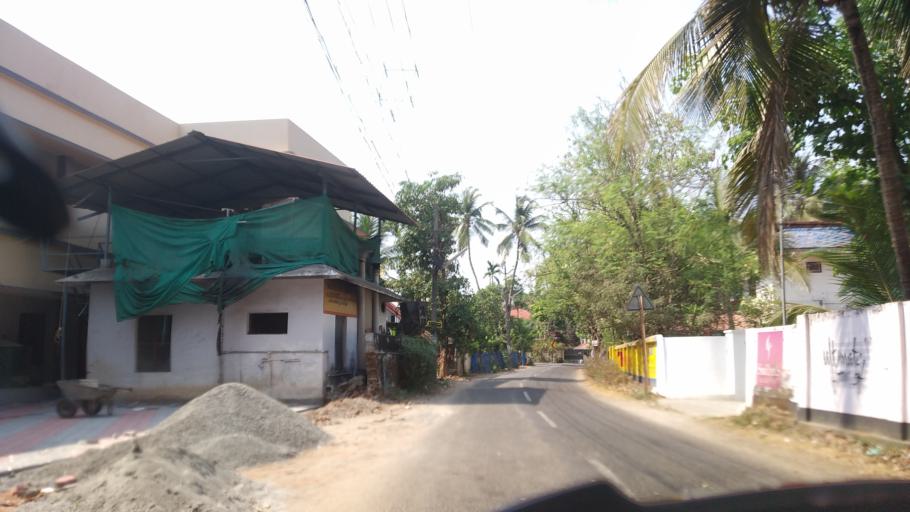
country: IN
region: Kerala
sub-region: Thrissur District
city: Thanniyam
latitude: 10.4095
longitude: 76.0944
